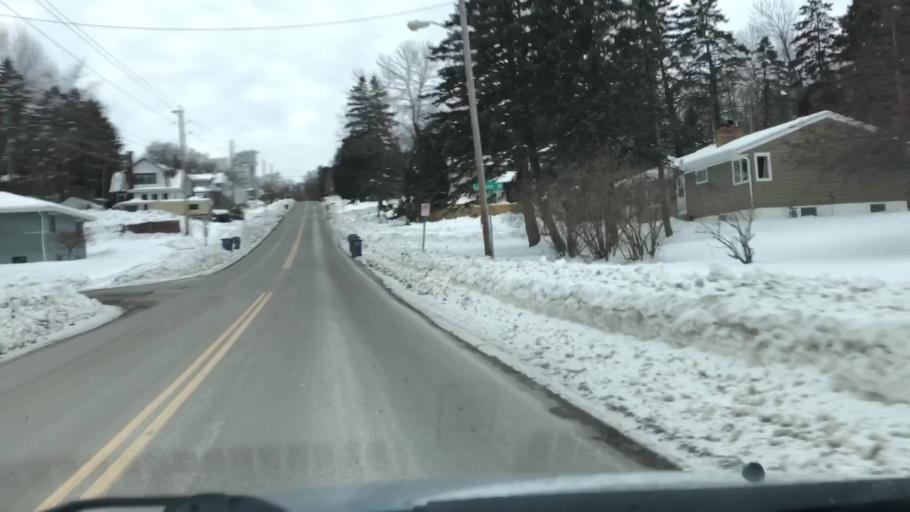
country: US
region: Minnesota
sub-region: Saint Louis County
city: Arnold
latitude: 46.8367
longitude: -92.0595
